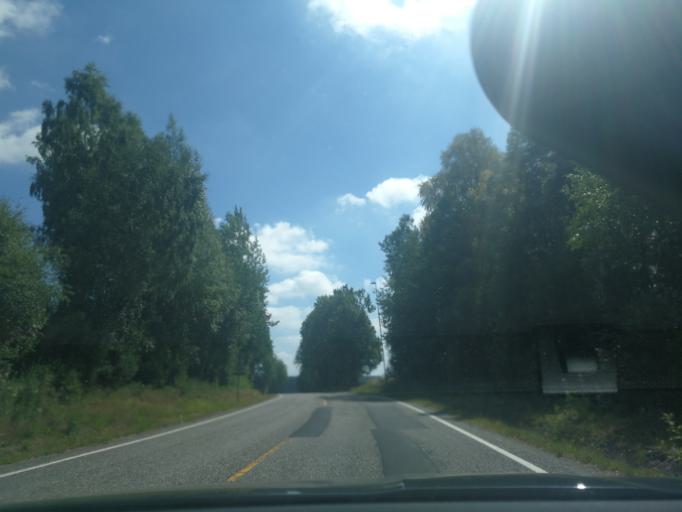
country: NO
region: Vestfold
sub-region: Stokke
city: Stokke
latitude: 59.2072
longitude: 10.2432
